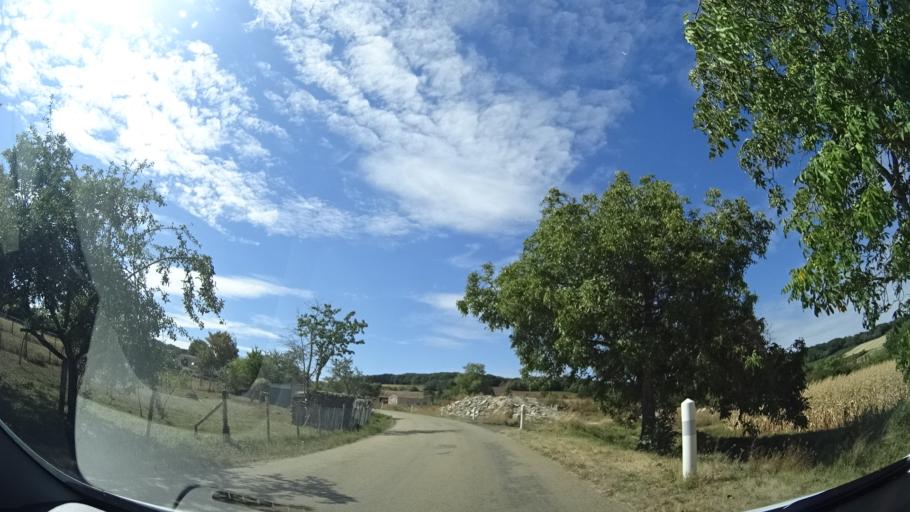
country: FR
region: Bourgogne
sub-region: Departement de l'Yonne
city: Aillant-sur-Tholon
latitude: 47.9184
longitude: 3.3309
